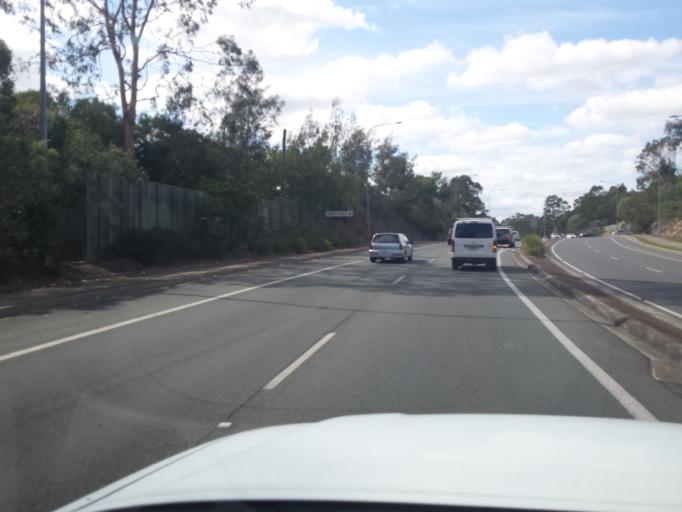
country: AU
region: Queensland
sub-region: Brisbane
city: Bridegman Downs
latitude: -27.3631
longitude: 152.9734
